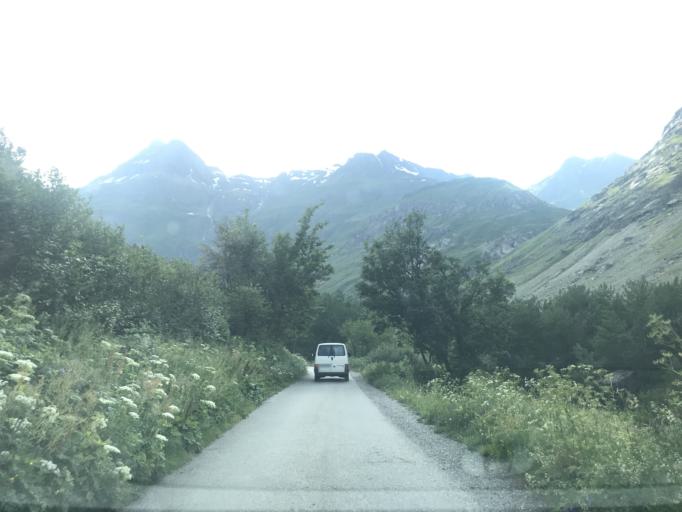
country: FR
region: Rhone-Alpes
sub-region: Departement de la Savoie
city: Val-d'Isere
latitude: 45.3732
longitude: 7.0671
